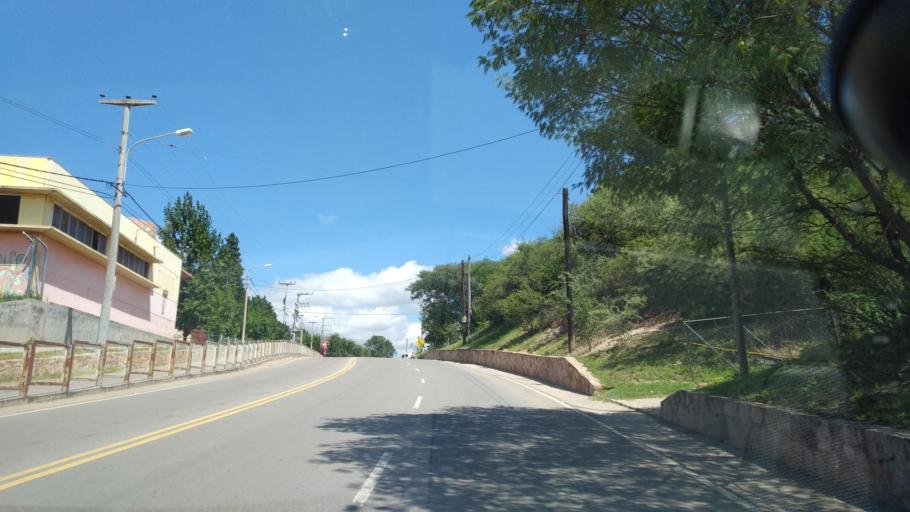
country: AR
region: Cordoba
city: Villa Cura Brochero
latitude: -31.7039
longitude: -65.0261
